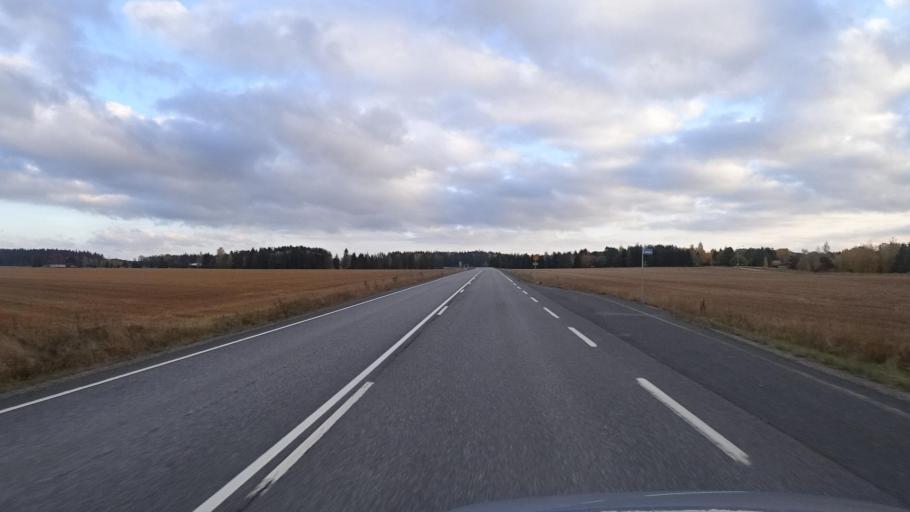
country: FI
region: Varsinais-Suomi
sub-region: Loimaa
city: Alastaro
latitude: 60.8874
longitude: 22.9716
